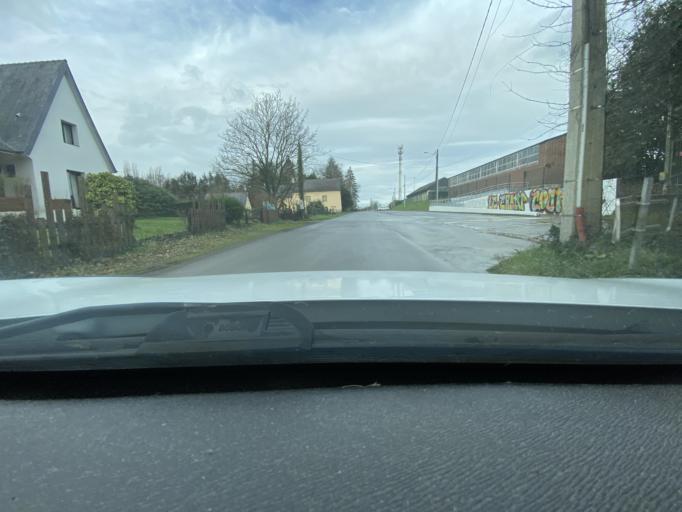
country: FR
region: Brittany
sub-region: Departement d'Ille-et-Vilaine
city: Melesse
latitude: 48.2176
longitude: -1.7087
